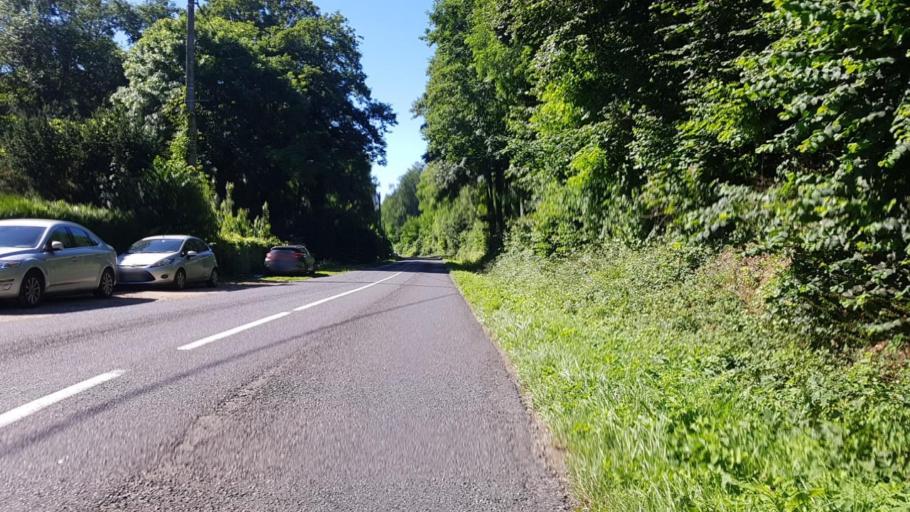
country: FR
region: Picardie
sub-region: Departement de l'Aisne
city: Chezy-sur-Marne
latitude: 48.9918
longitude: 3.3428
